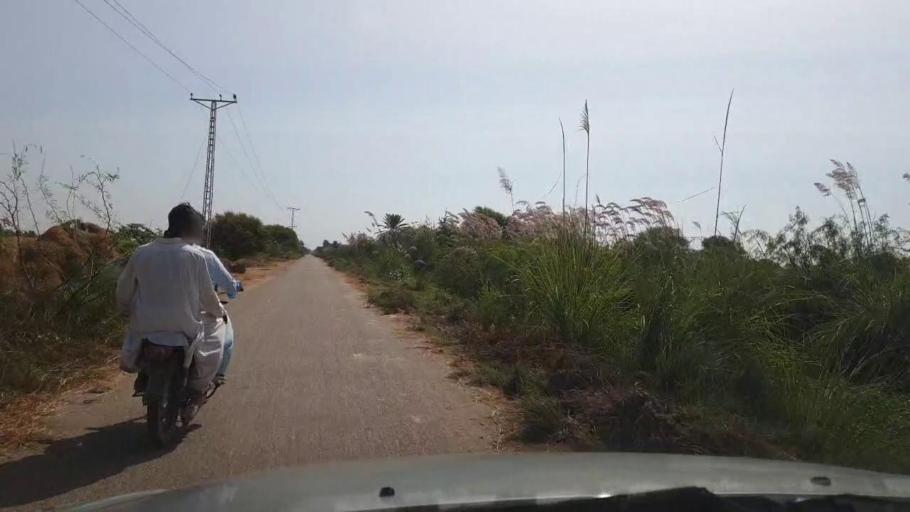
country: PK
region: Sindh
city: Tando Muhammad Khan
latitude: 25.1562
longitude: 68.3795
